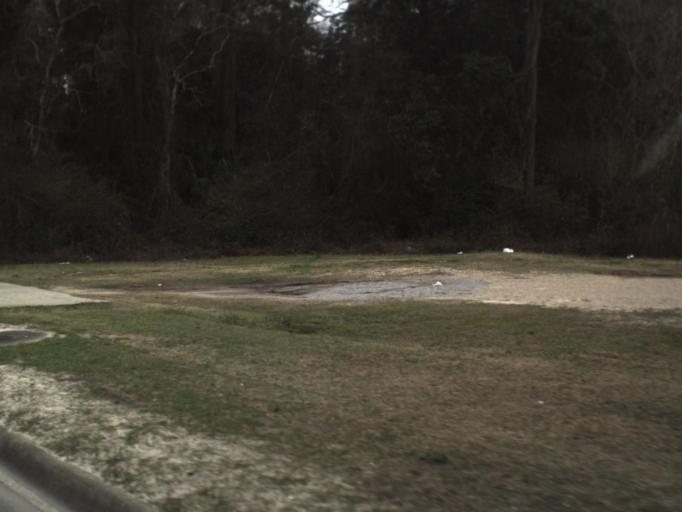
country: US
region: Florida
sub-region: Bay County
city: Springfield
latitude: 30.1687
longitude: -85.5912
